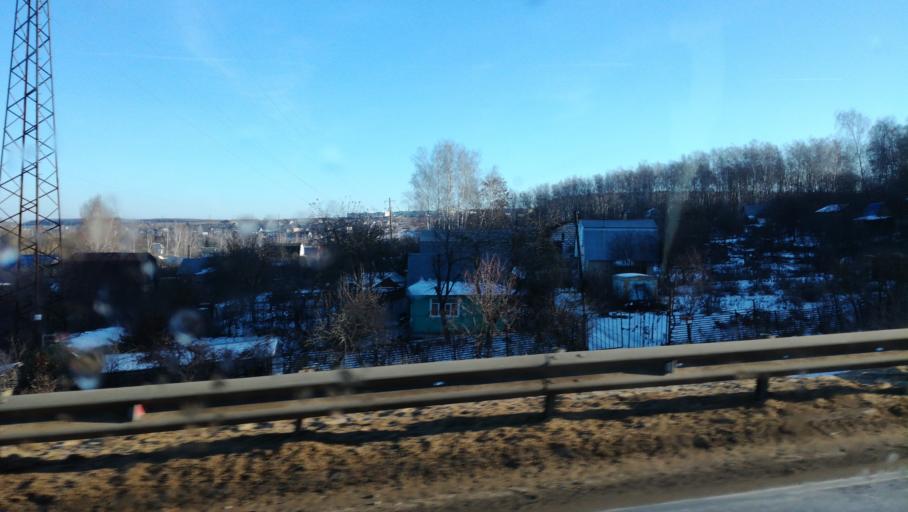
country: RU
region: Tula
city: Barsuki
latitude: 54.1748
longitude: 37.4545
